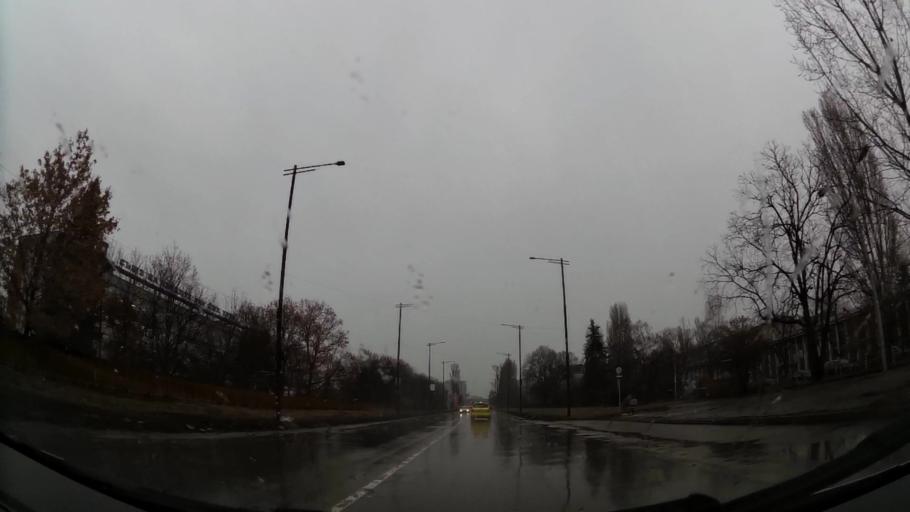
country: BG
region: Sofia-Capital
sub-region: Stolichna Obshtina
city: Sofia
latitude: 42.6729
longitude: 23.3879
